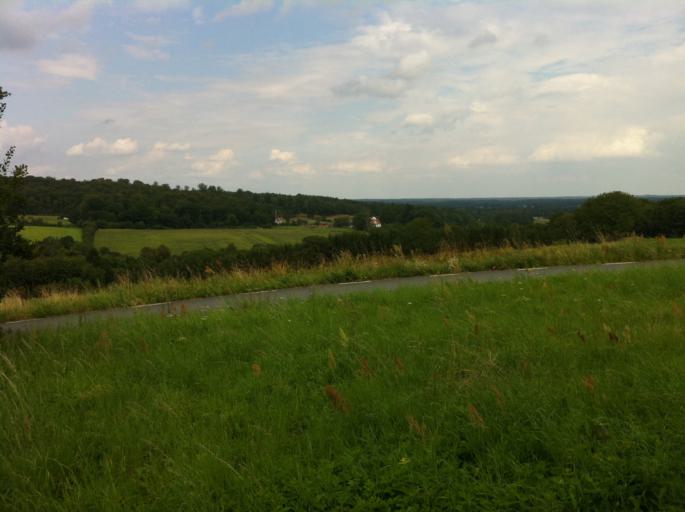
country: SE
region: Skane
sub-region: Hassleholms Kommun
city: Vinslov
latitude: 55.9452
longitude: 13.8557
